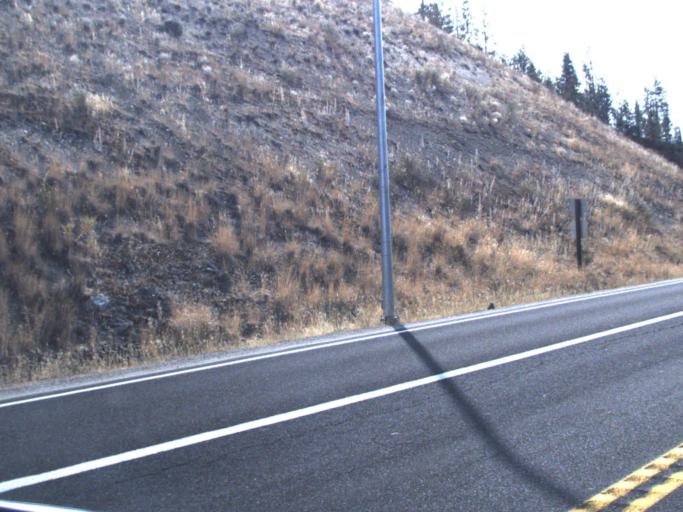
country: US
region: Washington
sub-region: Spokane County
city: Fairwood
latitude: 47.7763
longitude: -117.5437
